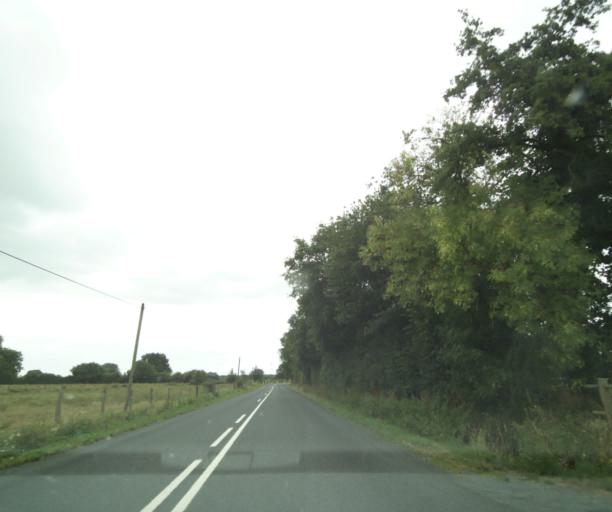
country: FR
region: Pays de la Loire
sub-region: Departement de la Sarthe
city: Precigne
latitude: 47.7550
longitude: -0.3066
